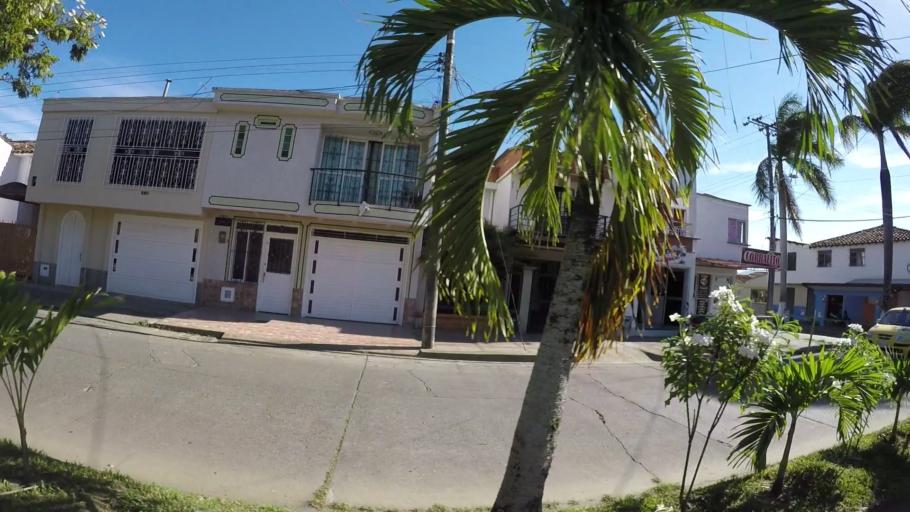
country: CO
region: Valle del Cauca
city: Cartago
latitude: 4.7583
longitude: -75.9216
